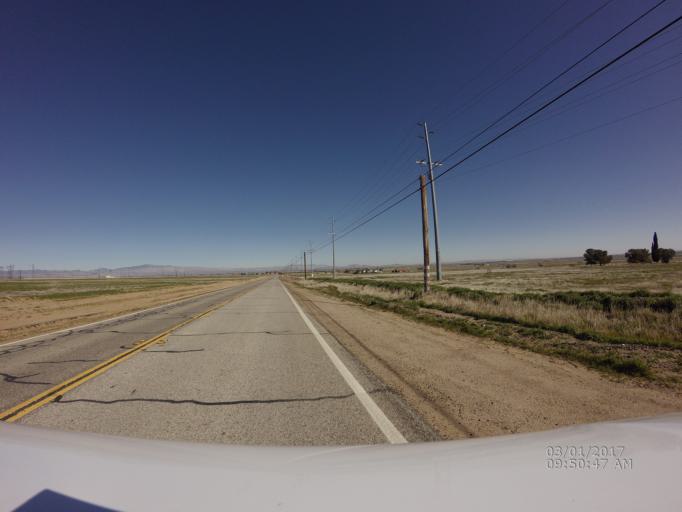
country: US
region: California
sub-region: Los Angeles County
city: Leona Valley
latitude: 34.6752
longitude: -118.2891
